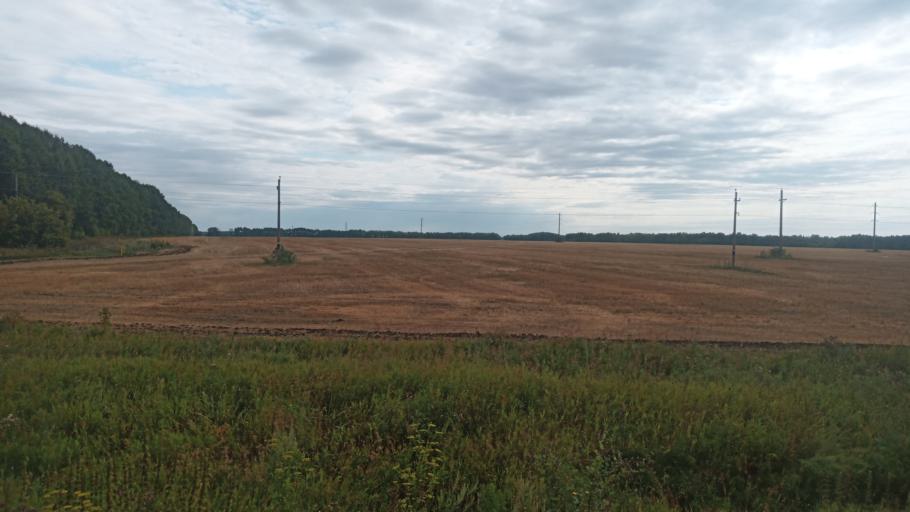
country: RU
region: Altai Krai
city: Nalobikha
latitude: 53.2400
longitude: 84.4570
